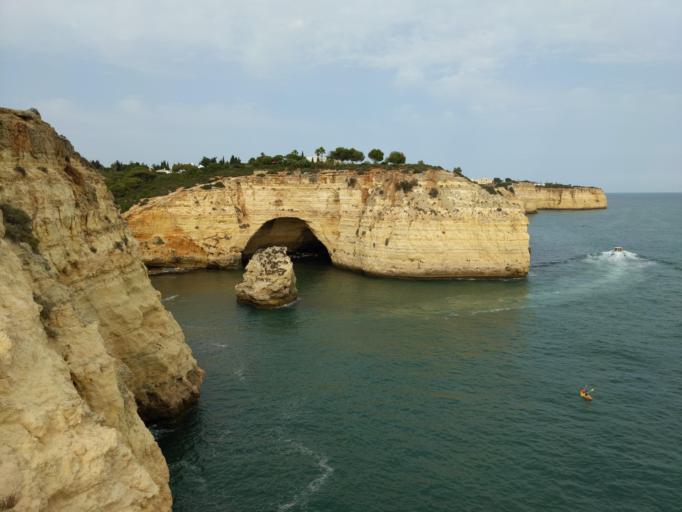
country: PT
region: Faro
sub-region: Lagoa
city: Carvoeiro
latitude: 37.0924
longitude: -8.4622
